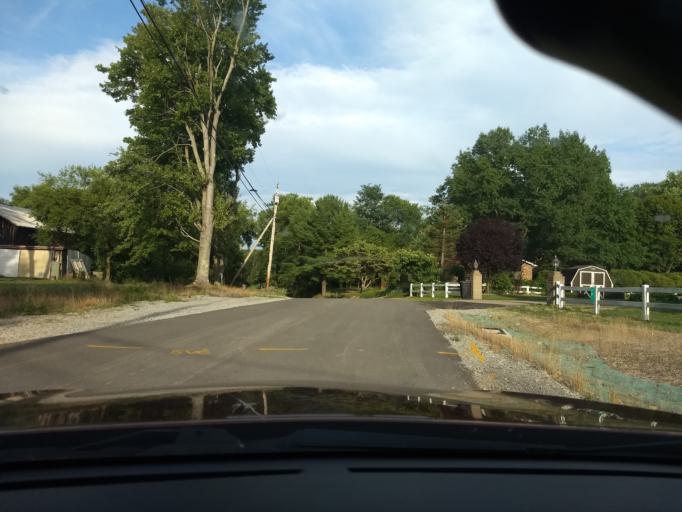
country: US
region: Pennsylvania
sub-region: Armstrong County
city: Freeport
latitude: 40.6603
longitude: -79.6729
